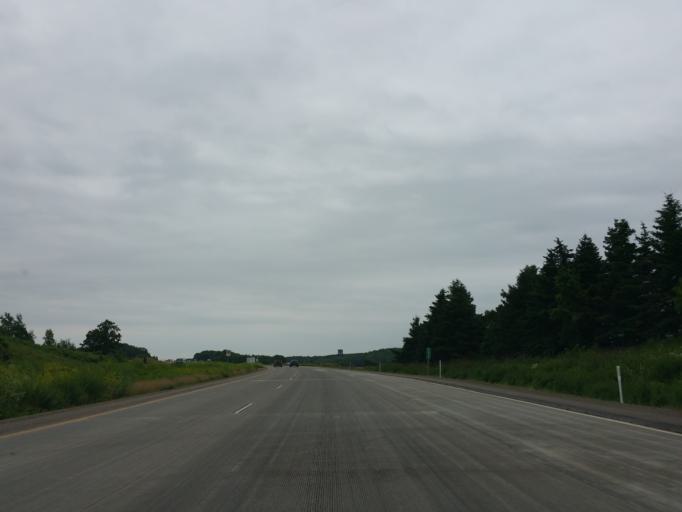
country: US
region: Wisconsin
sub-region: Trempealeau County
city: Osseo
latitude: 44.6373
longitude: -91.3012
